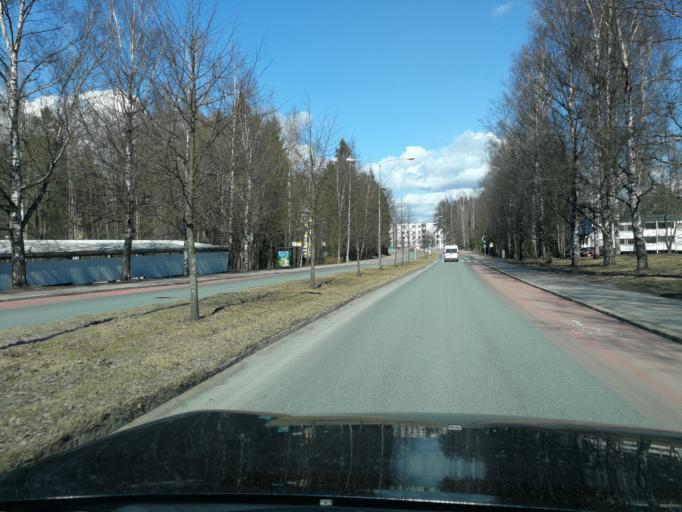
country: FI
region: Uusimaa
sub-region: Helsinki
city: Teekkarikylae
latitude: 60.2346
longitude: 24.8466
